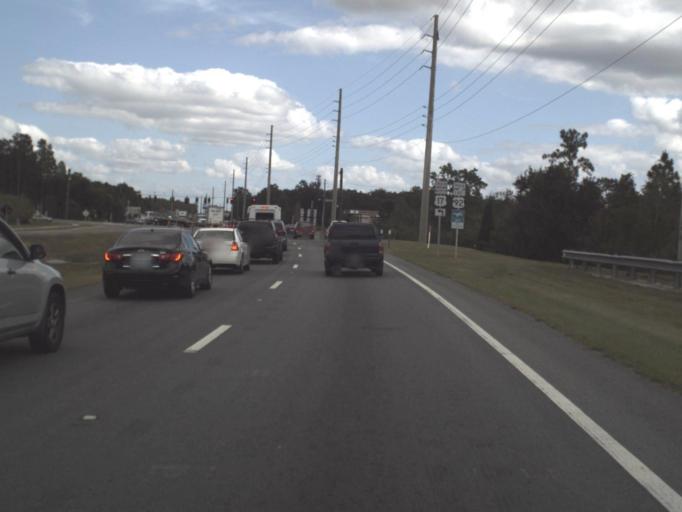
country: US
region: Florida
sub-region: Orange County
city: Hunters Creek
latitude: 28.3373
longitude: -81.4060
